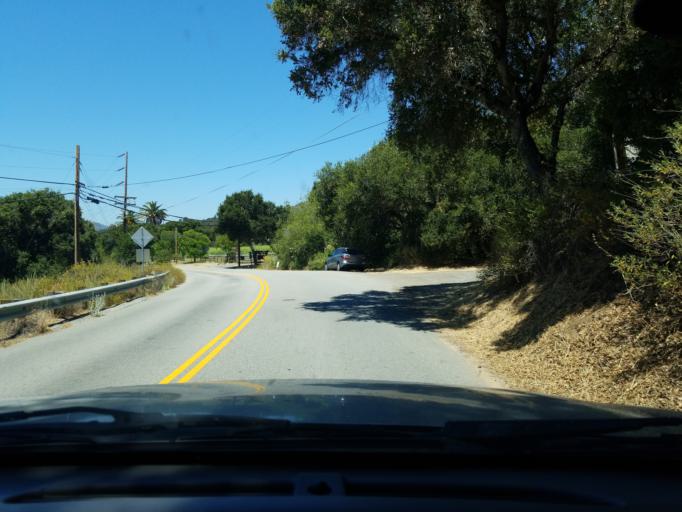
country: US
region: California
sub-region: Monterey County
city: Carmel Valley Village
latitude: 36.4699
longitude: -121.7137
